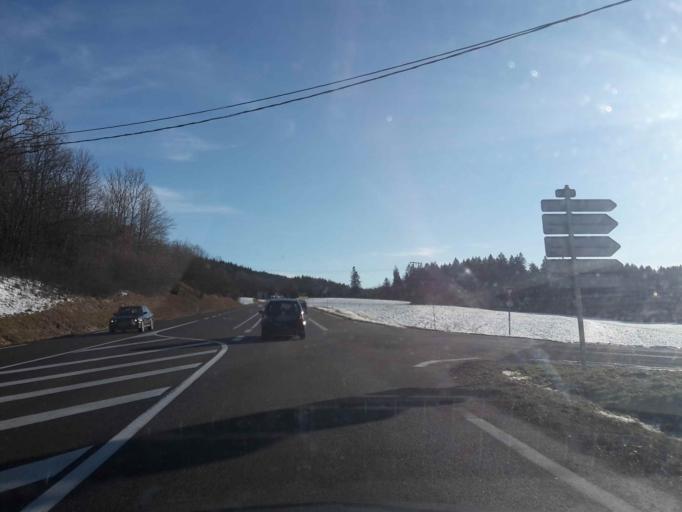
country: FR
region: Franche-Comte
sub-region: Departement du Doubs
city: Doubs
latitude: 47.0162
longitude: 6.3255
